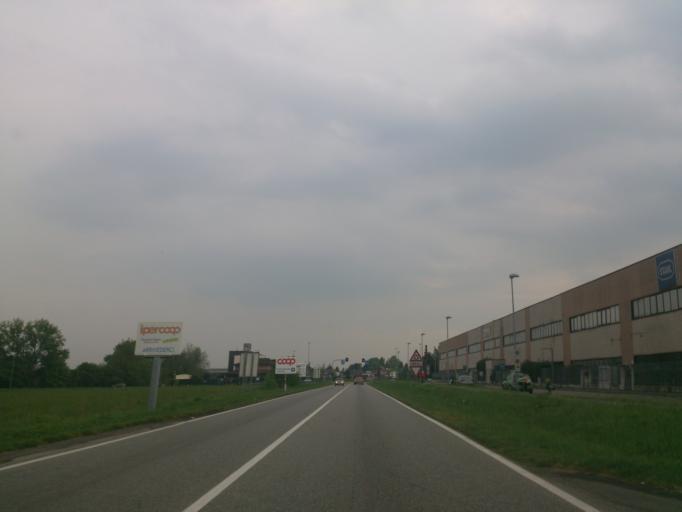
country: IT
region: Lombardy
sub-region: Citta metropolitana di Milano
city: Mezzate
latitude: 45.4459
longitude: 9.2876
